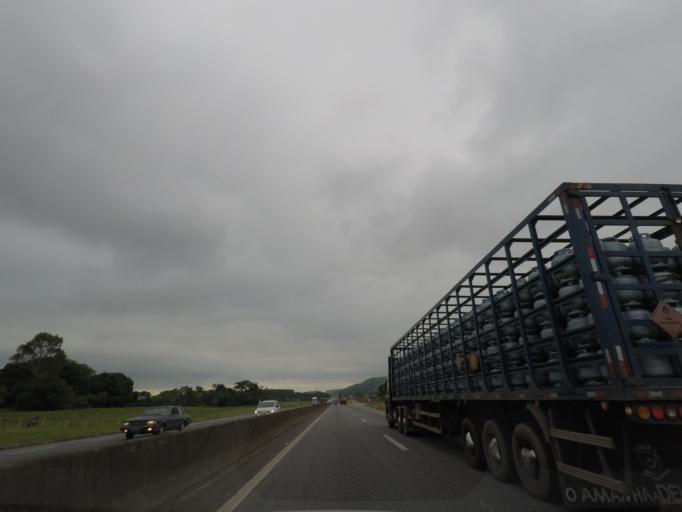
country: BR
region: Sao Paulo
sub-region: Aparecida
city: Aparecida
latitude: -22.8985
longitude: -45.3010
